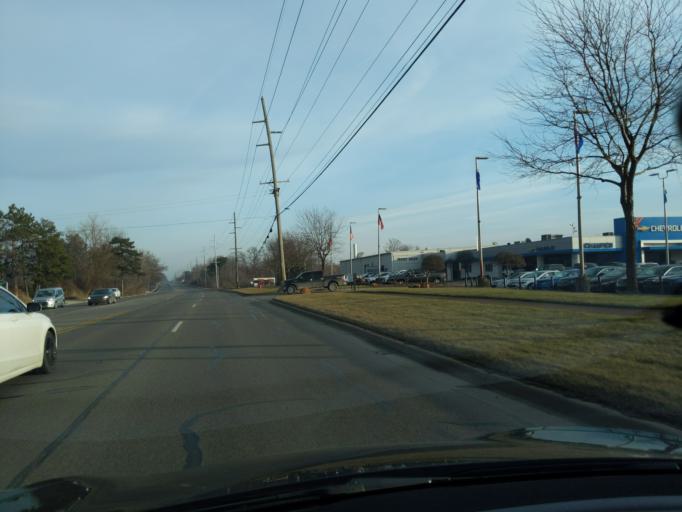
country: US
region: Michigan
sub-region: Livingston County
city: Howell
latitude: 42.5800
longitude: -83.8552
